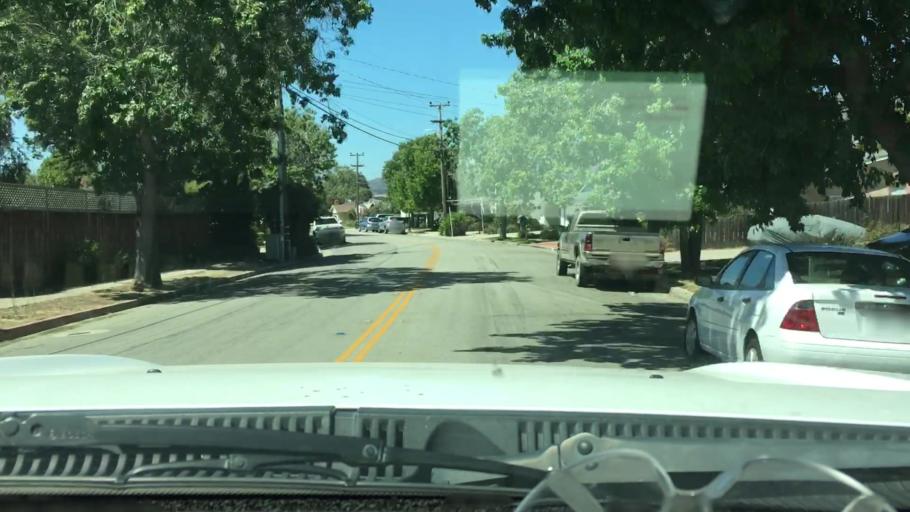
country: US
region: California
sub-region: San Luis Obispo County
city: San Luis Obispo
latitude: 35.2602
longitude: -120.6846
